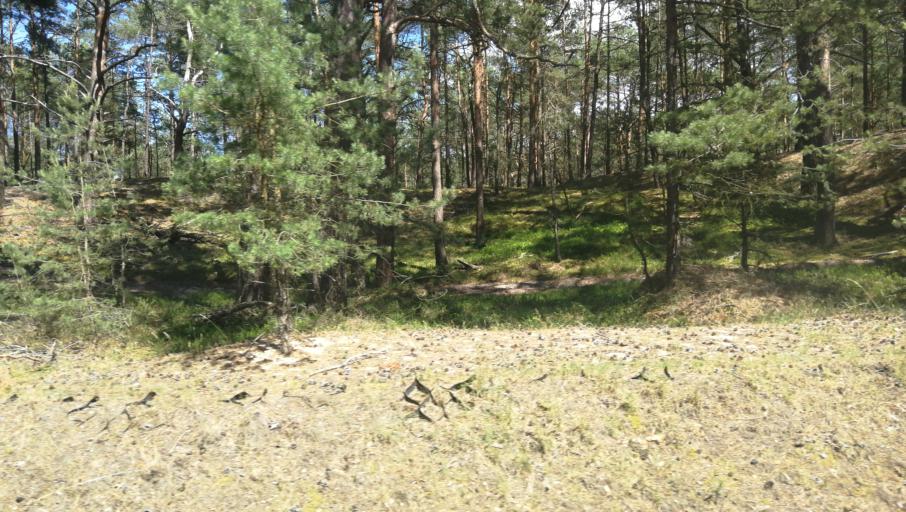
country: PL
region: Pomeranian Voivodeship
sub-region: Powiat pucki
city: Hel
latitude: 54.6308
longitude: 18.8027
